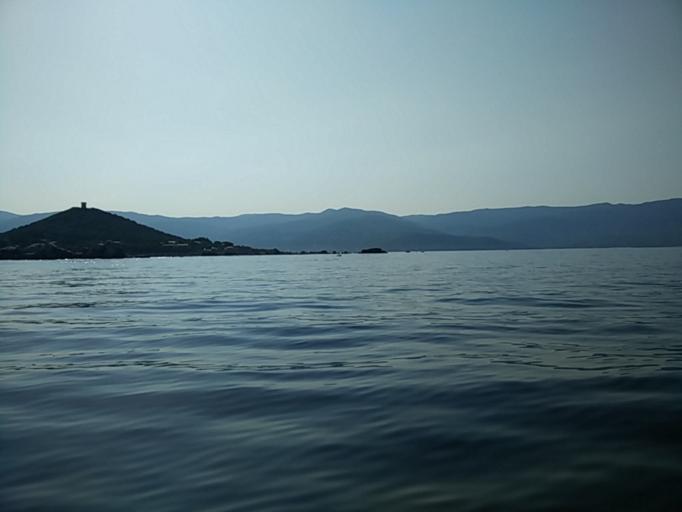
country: FR
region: Corsica
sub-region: Departement de la Corse-du-Sud
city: Ajaccio
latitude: 41.8457
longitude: 8.7443
